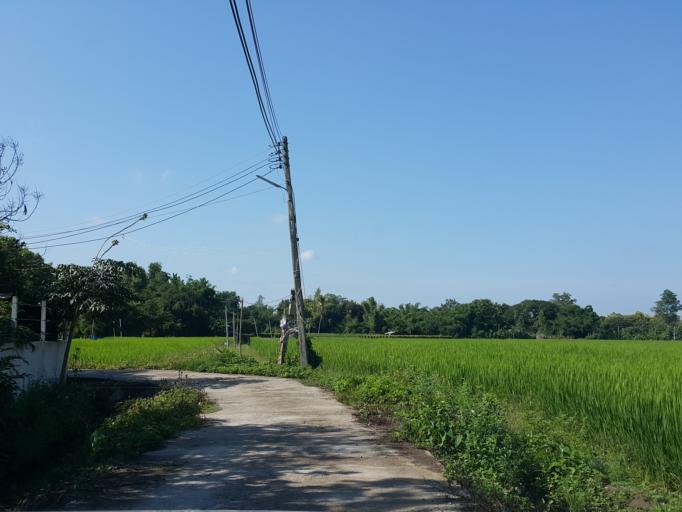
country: TH
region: Chiang Mai
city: San Kamphaeng
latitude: 18.8213
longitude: 99.1651
